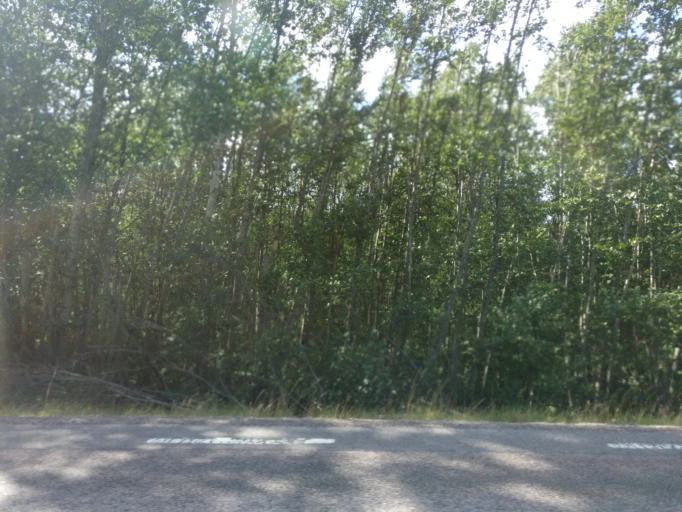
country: SE
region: Vaermland
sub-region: Hagfors Kommun
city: Ekshaerad
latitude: 60.3706
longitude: 13.3041
